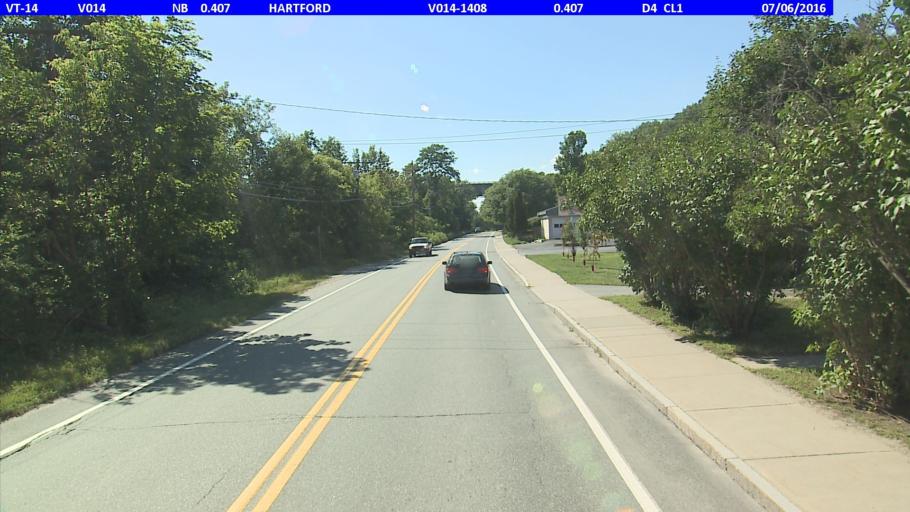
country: US
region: Vermont
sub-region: Windsor County
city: White River Junction
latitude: 43.6545
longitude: -72.3268
